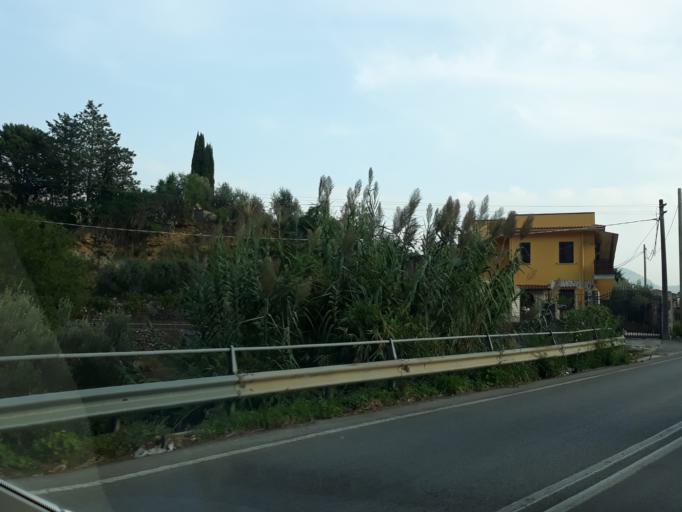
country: IT
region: Sicily
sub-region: Palermo
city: Cannizzaro-Favara
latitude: 38.0695
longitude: 13.2690
